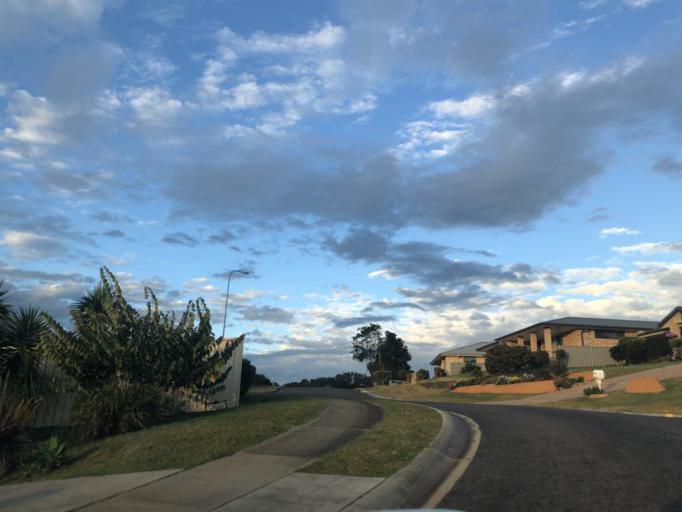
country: AU
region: New South Wales
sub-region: Nambucca Shire
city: Macksville
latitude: -30.7317
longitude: 152.9092
